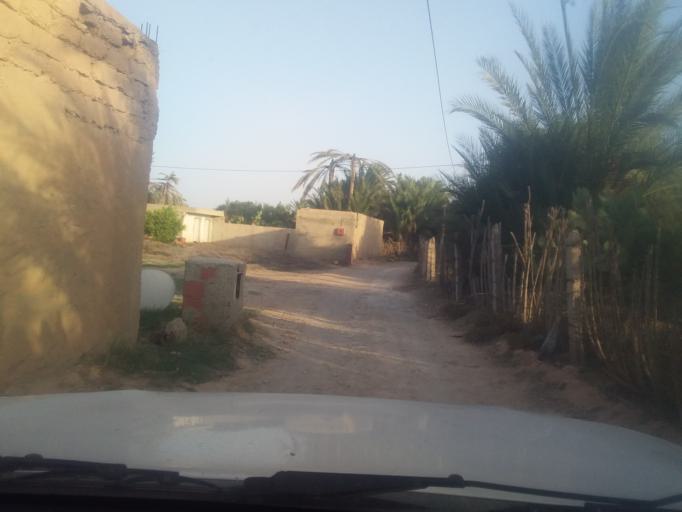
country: TN
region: Qabis
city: Gabes
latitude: 33.6300
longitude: 10.2953
